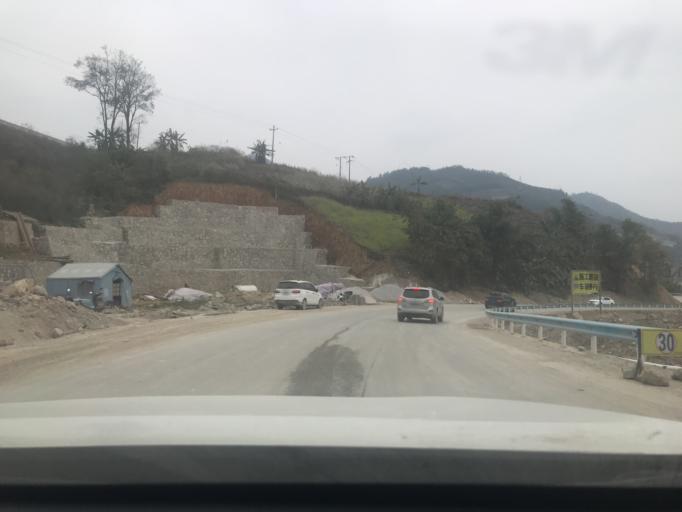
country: CN
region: Guangxi Zhuangzu Zizhiqu
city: Xinzhou
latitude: 25.0138
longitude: 105.8603
